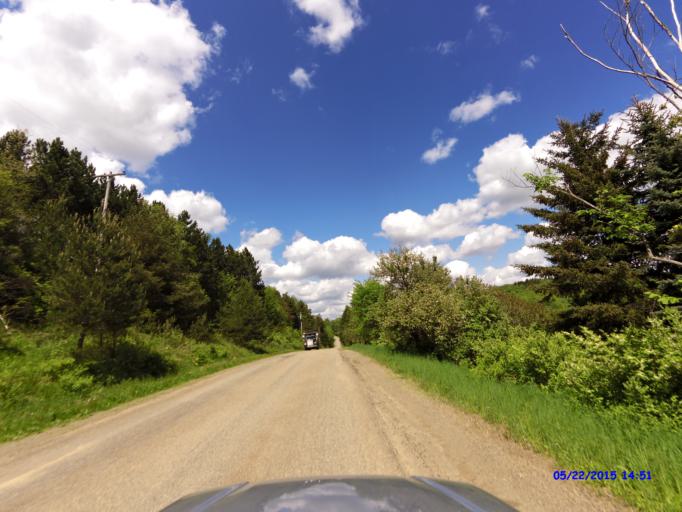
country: US
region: New York
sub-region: Cattaraugus County
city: Franklinville
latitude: 42.3746
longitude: -78.5768
